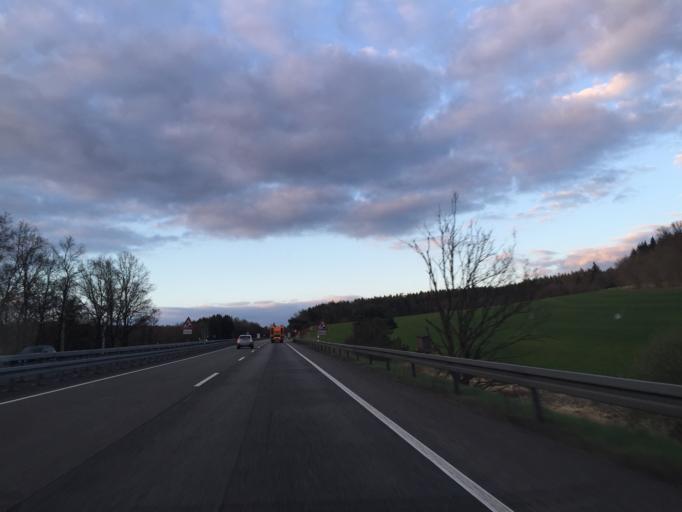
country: DE
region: Hesse
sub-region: Regierungsbezirk Kassel
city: Friedewald
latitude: 50.8745
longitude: 9.7889
